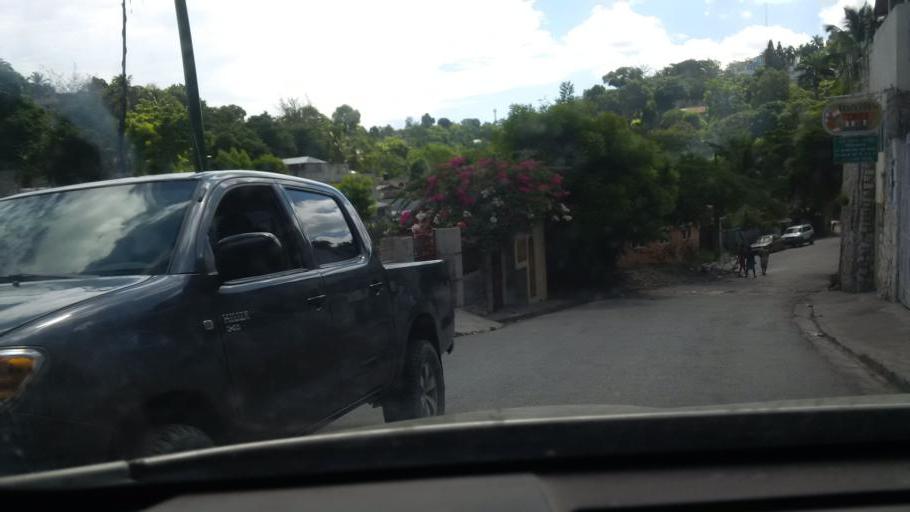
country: HT
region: Ouest
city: Delmas 73
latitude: 18.5400
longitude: -72.3166
